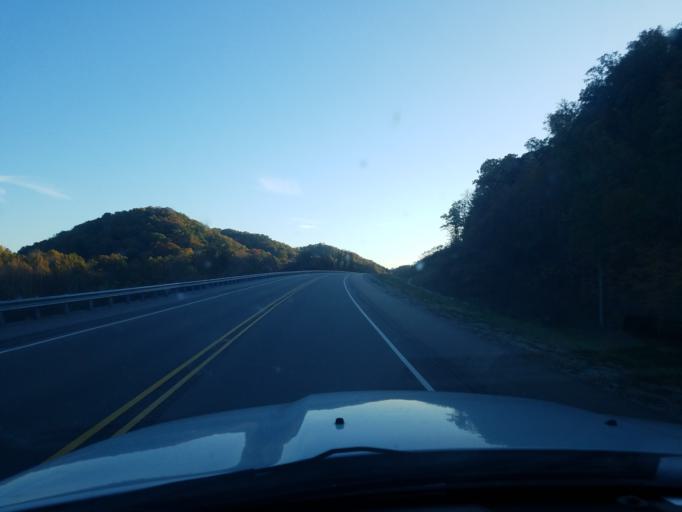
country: US
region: Indiana
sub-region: Washington County
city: New Pekin
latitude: 38.4504
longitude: -85.9344
